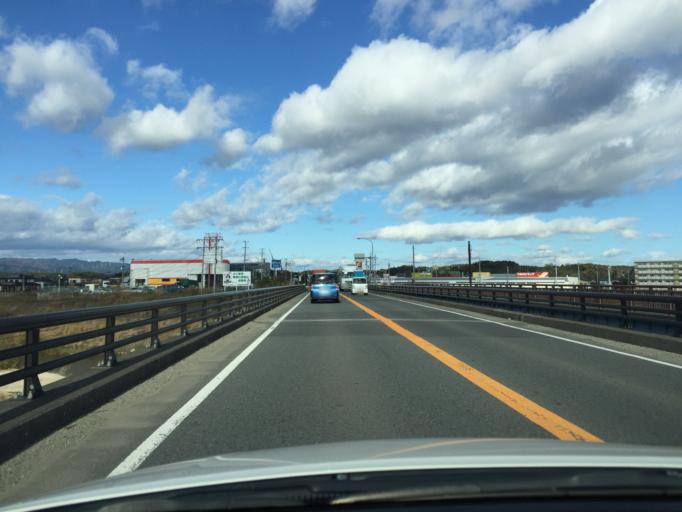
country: JP
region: Fukushima
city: Namie
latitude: 37.4897
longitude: 141.0047
